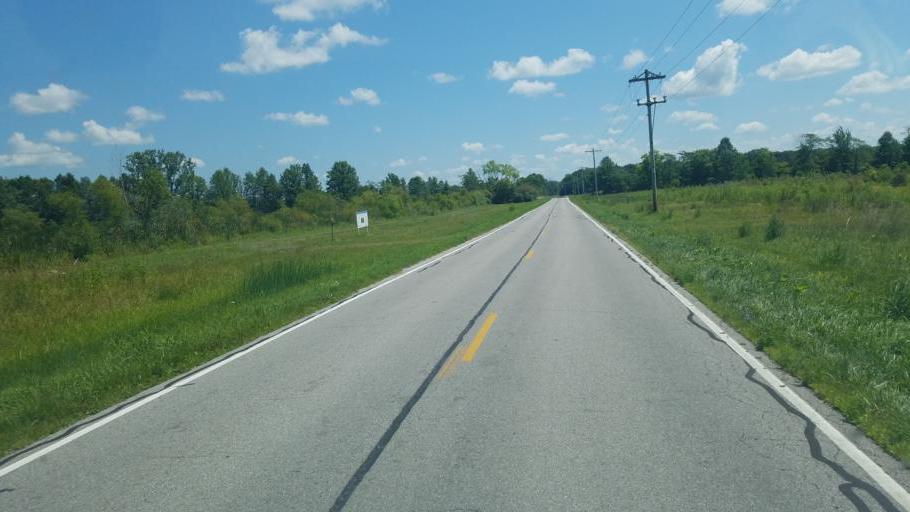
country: US
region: Ohio
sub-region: Union County
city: Richwood
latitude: 40.5712
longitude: -83.3109
